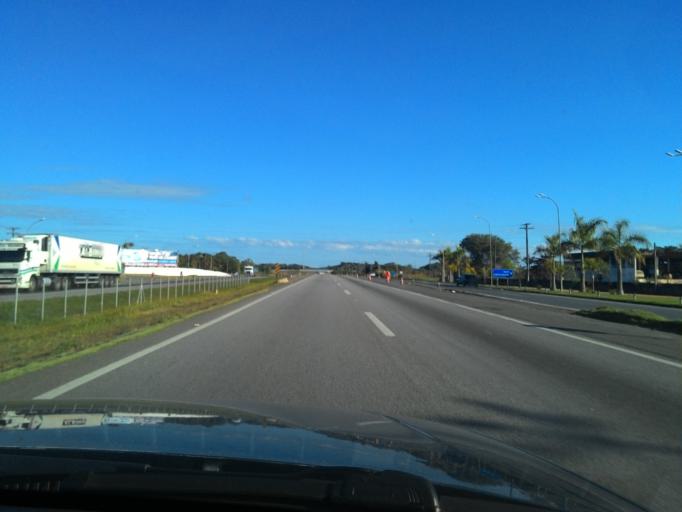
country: BR
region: Sao Paulo
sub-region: Registro
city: Registro
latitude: -24.5311
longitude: -47.8571
